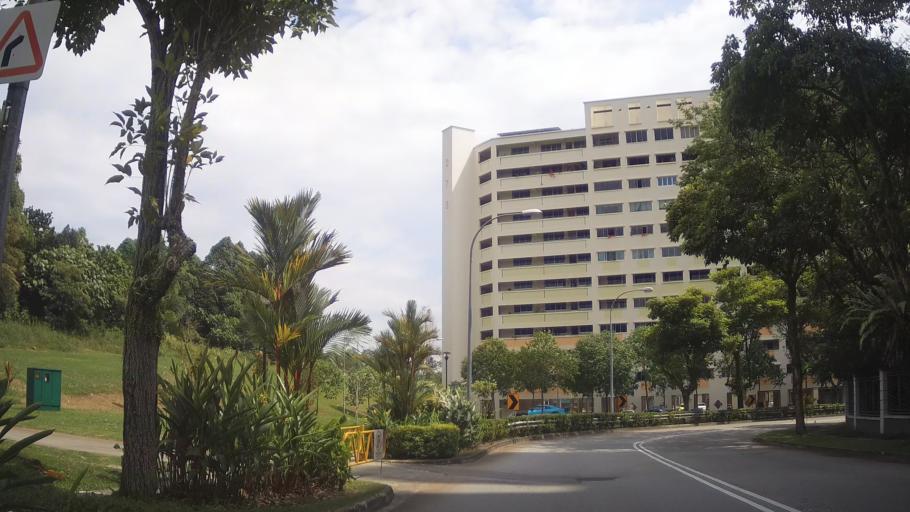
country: MY
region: Johor
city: Johor Bahru
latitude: 1.3788
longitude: 103.7750
